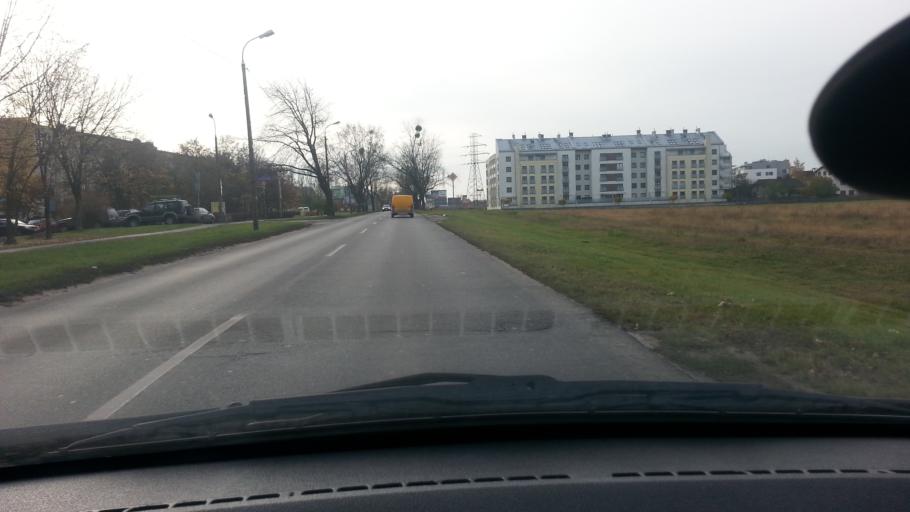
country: PL
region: Masovian Voivodeship
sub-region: Warszawa
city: Bemowo
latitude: 52.2345
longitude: 20.8967
